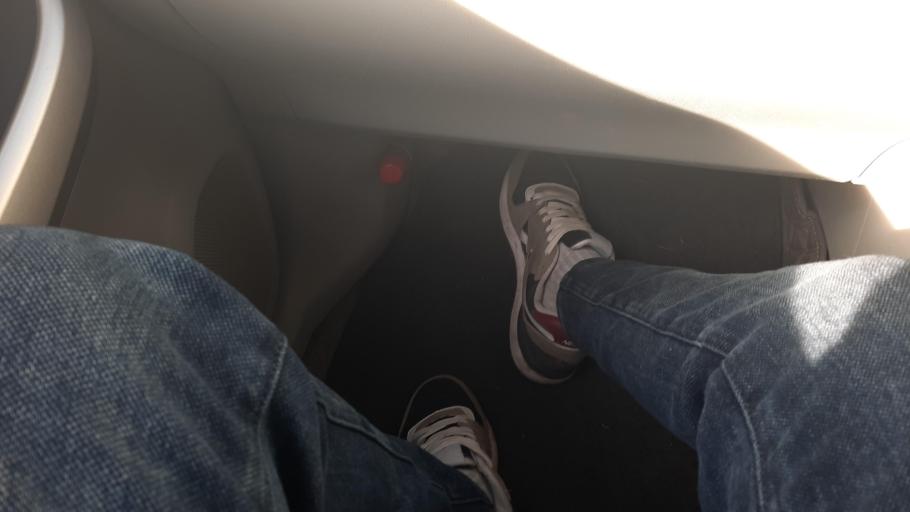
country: MN
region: Orhon
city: Erdenet
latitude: 49.0322
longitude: 104.0542
